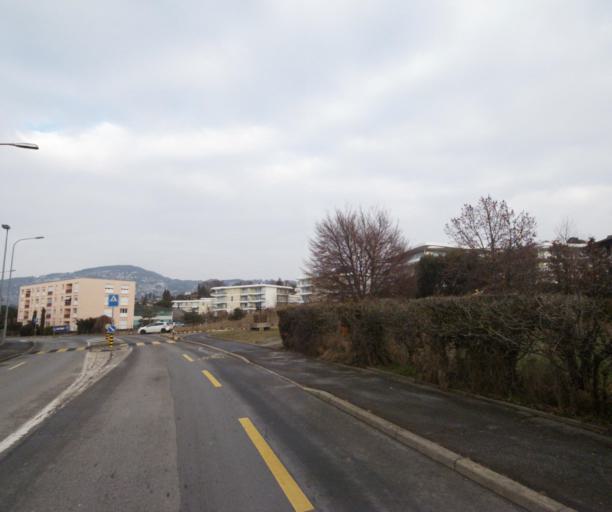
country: CH
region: Vaud
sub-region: Riviera-Pays-d'Enhaut District
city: La Tour-de-Peilz
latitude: 46.4563
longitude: 6.8664
